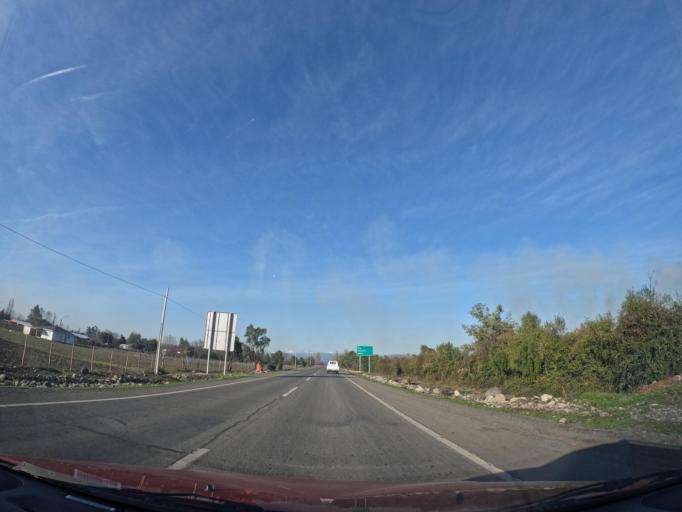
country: CL
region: Maule
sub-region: Provincia de Linares
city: Colbun
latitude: -35.6277
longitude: -71.4618
